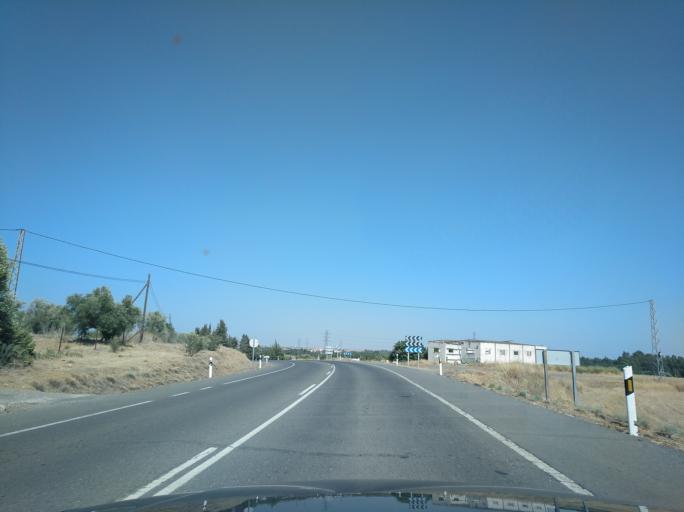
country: ES
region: Andalusia
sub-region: Provincia de Huelva
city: Gibraleon
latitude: 37.3563
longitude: -6.9974
